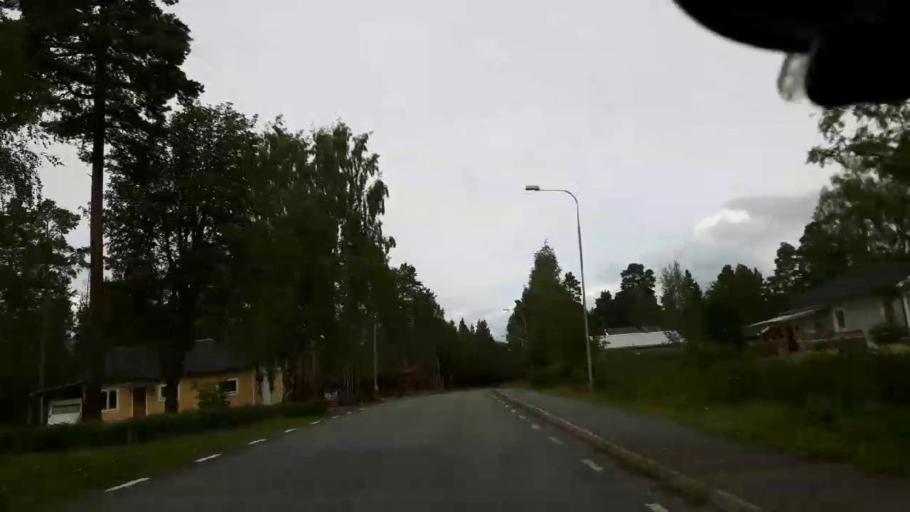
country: SE
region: Jaemtland
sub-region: Krokoms Kommun
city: Valla
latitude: 63.4603
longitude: 14.0618
